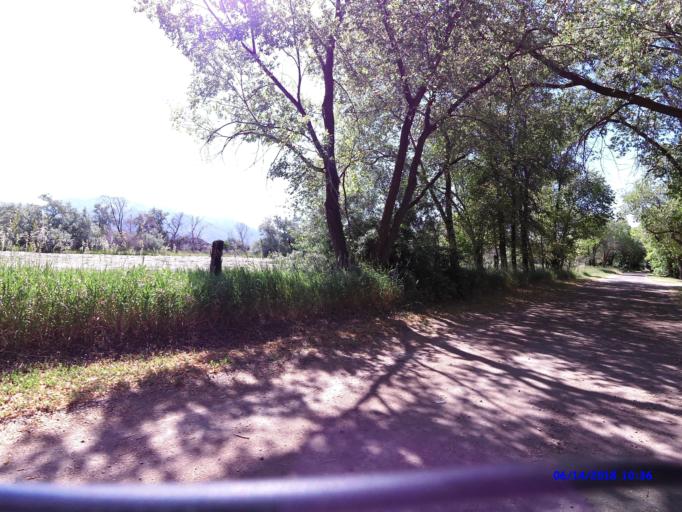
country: US
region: Utah
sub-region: Weber County
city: Riverdale
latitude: 41.2118
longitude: -112.0144
